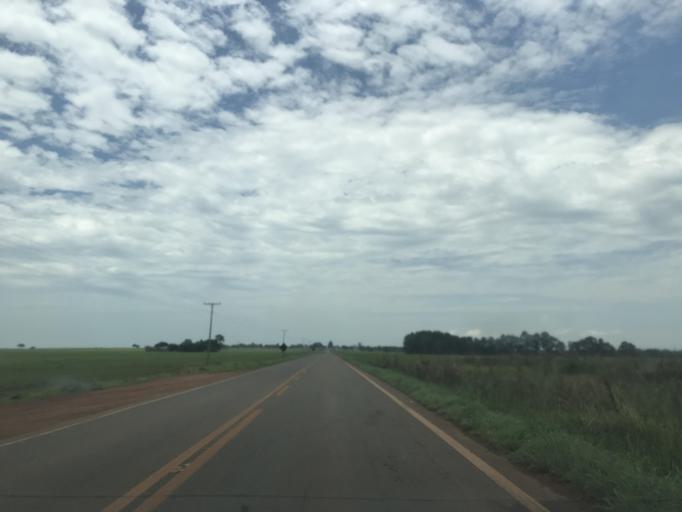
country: BR
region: Goias
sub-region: Luziania
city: Luziania
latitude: -16.2943
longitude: -48.0078
